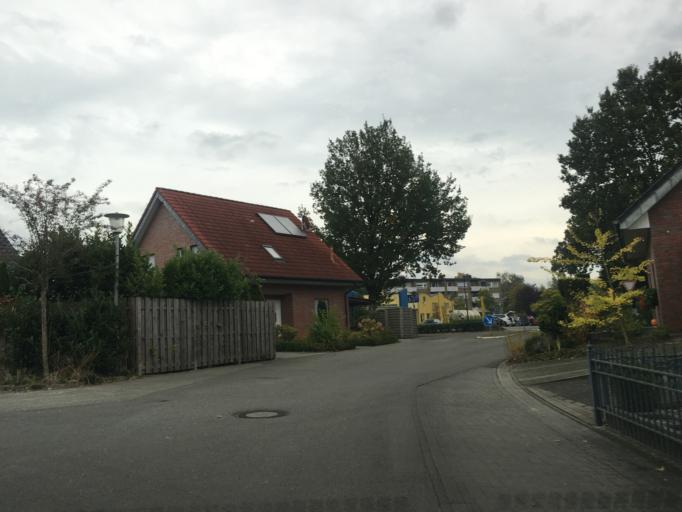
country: DE
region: North Rhine-Westphalia
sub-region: Regierungsbezirk Munster
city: Steinfurt
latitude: 52.1390
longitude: 7.3239
